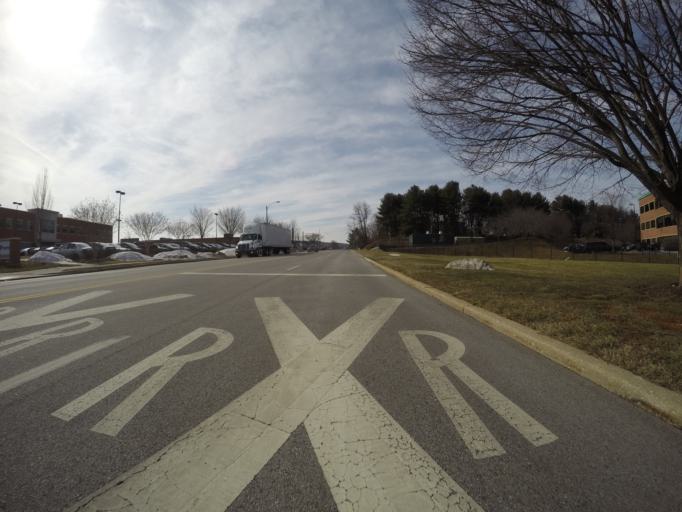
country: US
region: Maryland
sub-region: Baltimore County
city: Cockeysville
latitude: 39.4922
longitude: -76.6569
